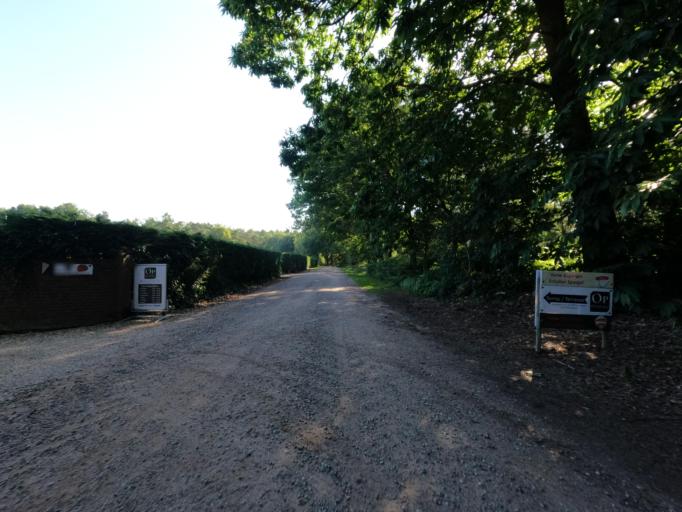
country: NL
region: Limburg
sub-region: Gemeente Roerdalen
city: Vlodrop
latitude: 51.1191
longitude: 6.0637
